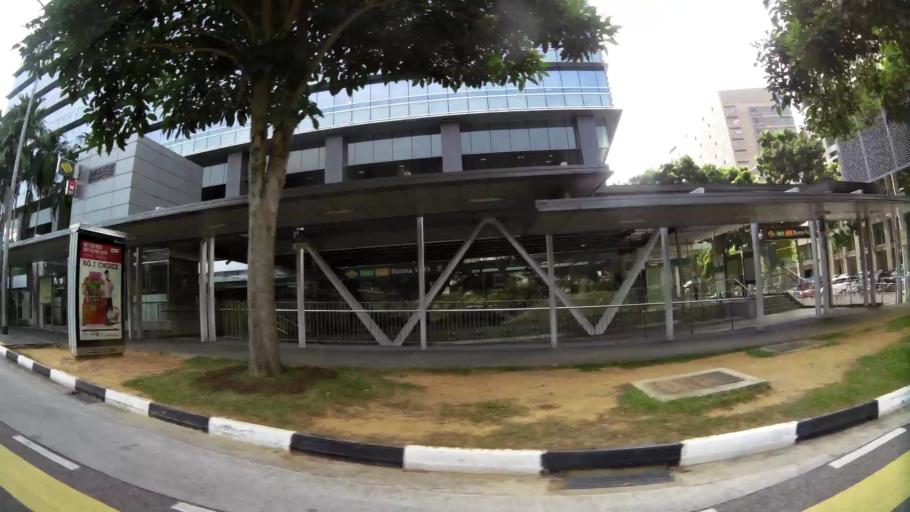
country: SG
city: Singapore
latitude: 1.3062
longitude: 103.7907
